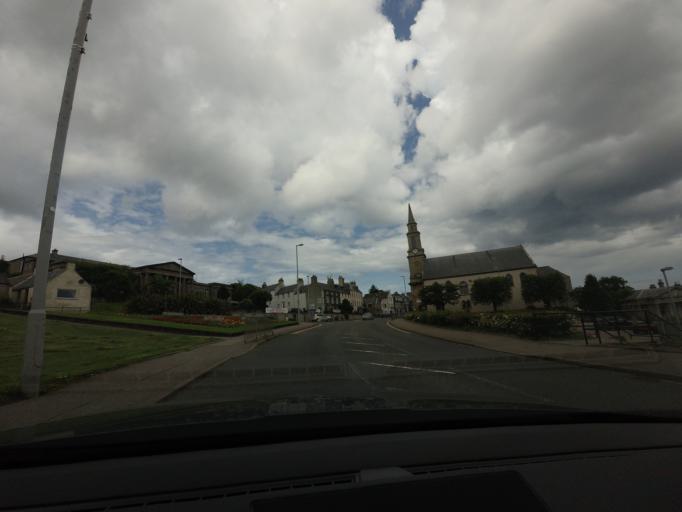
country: GB
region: Scotland
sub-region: Aberdeenshire
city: Banff
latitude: 57.6622
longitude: -2.5231
